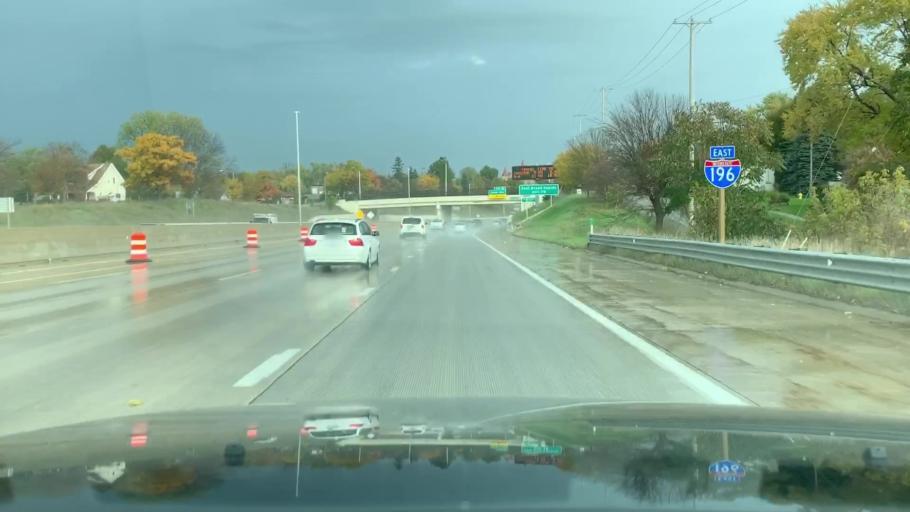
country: US
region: Michigan
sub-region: Kent County
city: Grand Rapids
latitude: 42.9728
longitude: -85.6520
